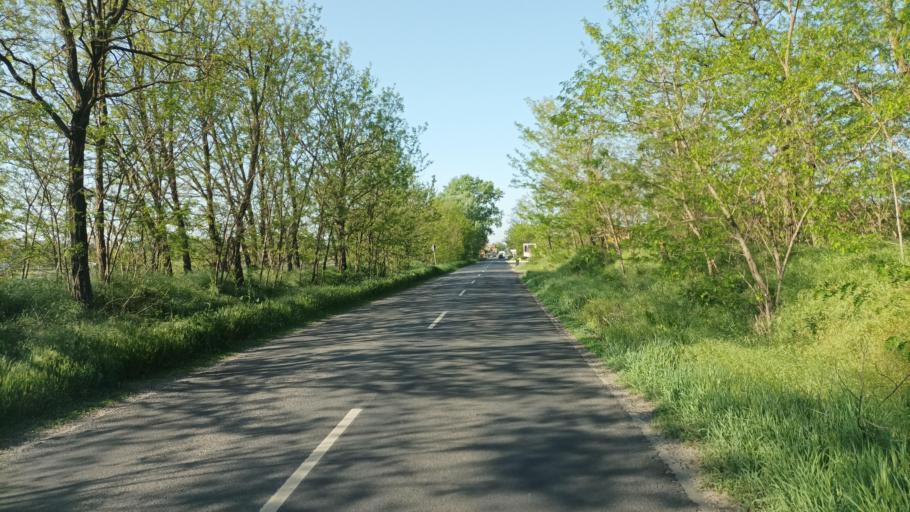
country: HU
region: Pest
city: Monor
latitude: 47.3041
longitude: 19.4364
